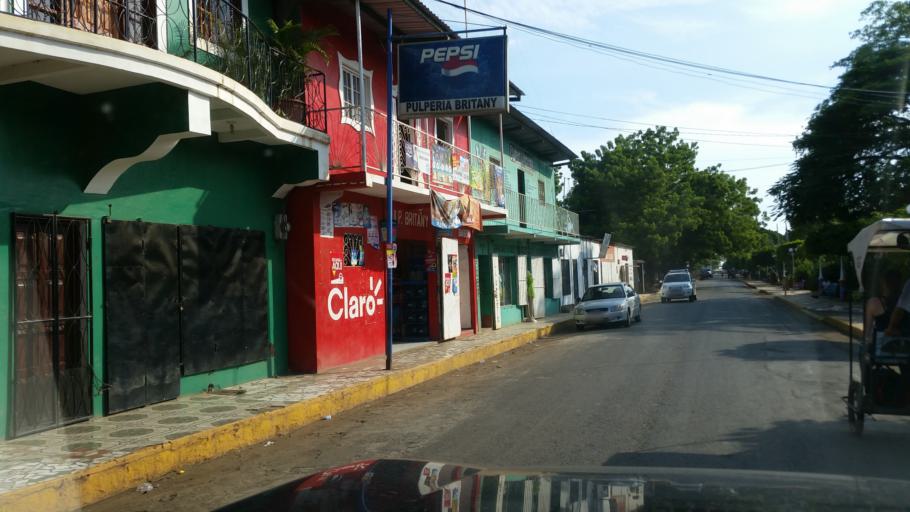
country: NI
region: Managua
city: Masachapa
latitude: 11.7858
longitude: -86.5128
